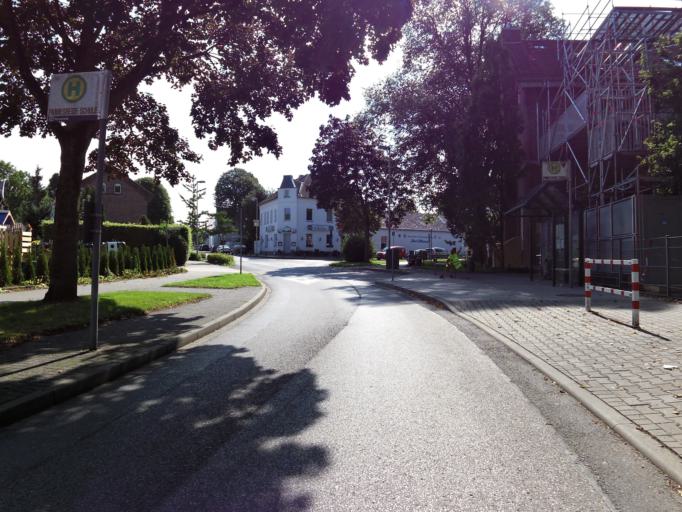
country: NL
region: Limburg
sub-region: Gemeente Kerkrade
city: Kerkrade
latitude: 50.8470
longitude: 6.0685
